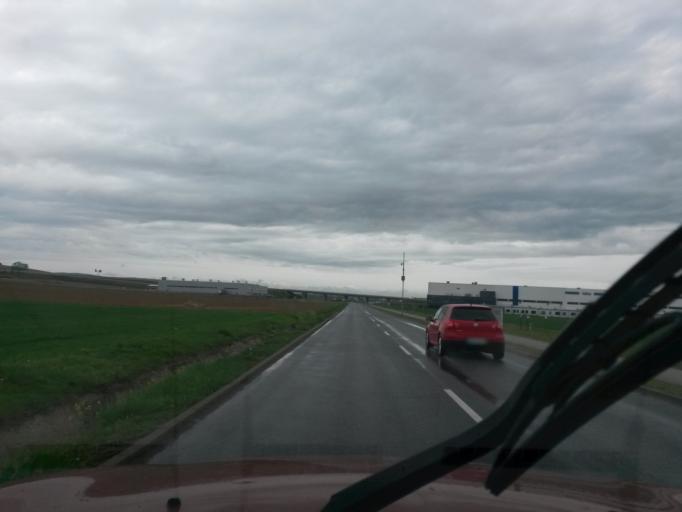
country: HU
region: Borsod-Abauj-Zemplen
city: Gonc
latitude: 48.5499
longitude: 21.2404
